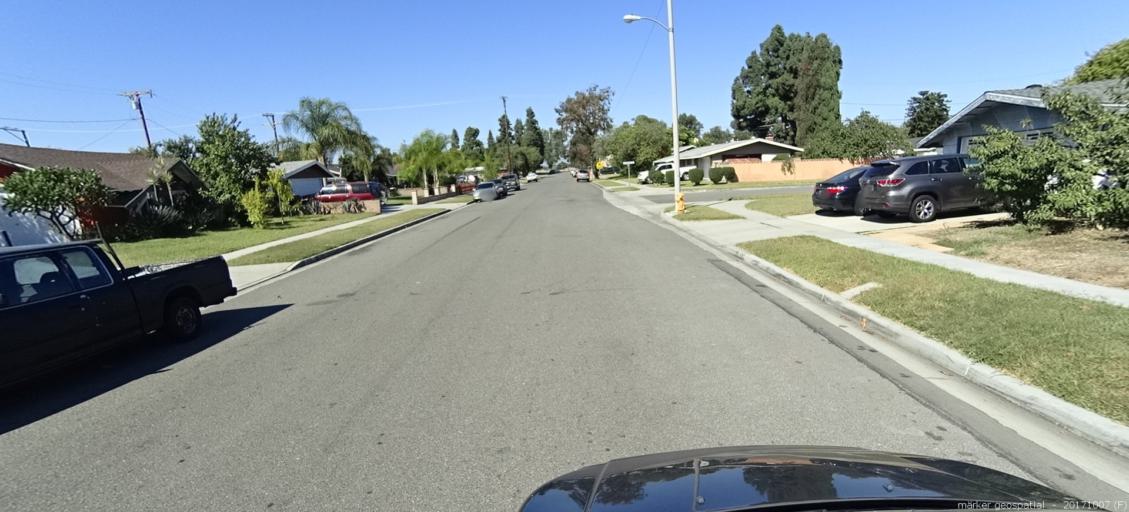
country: US
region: California
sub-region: Orange County
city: Stanton
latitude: 33.7786
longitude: -117.9862
